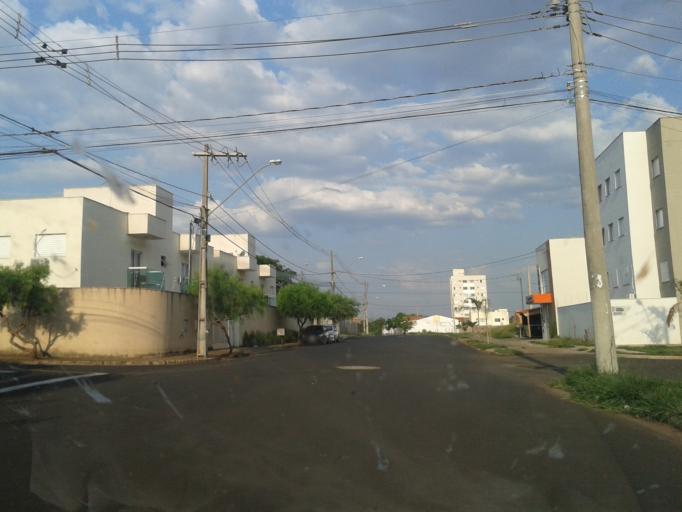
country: BR
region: Minas Gerais
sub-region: Uberlandia
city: Uberlandia
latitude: -18.9666
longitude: -48.3149
